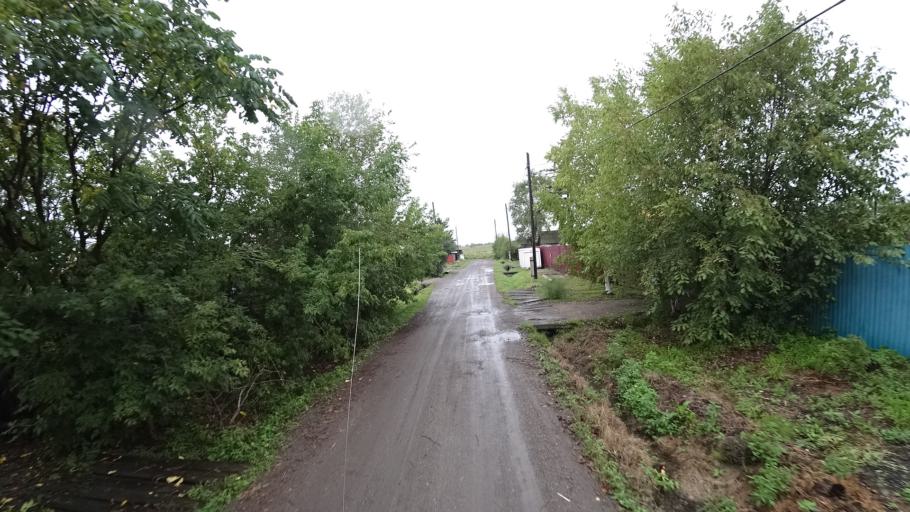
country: RU
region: Primorskiy
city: Monastyrishche
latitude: 44.2016
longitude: 132.4206
